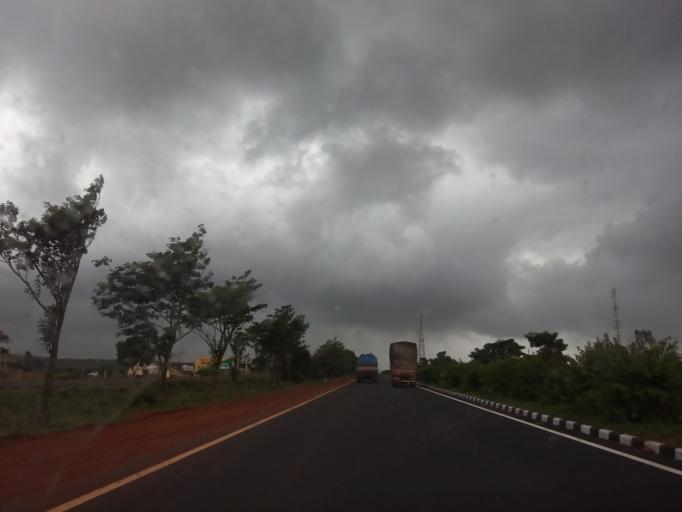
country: IN
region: Karnataka
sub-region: Belgaum
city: Belgaum
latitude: 16.0236
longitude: 74.5224
